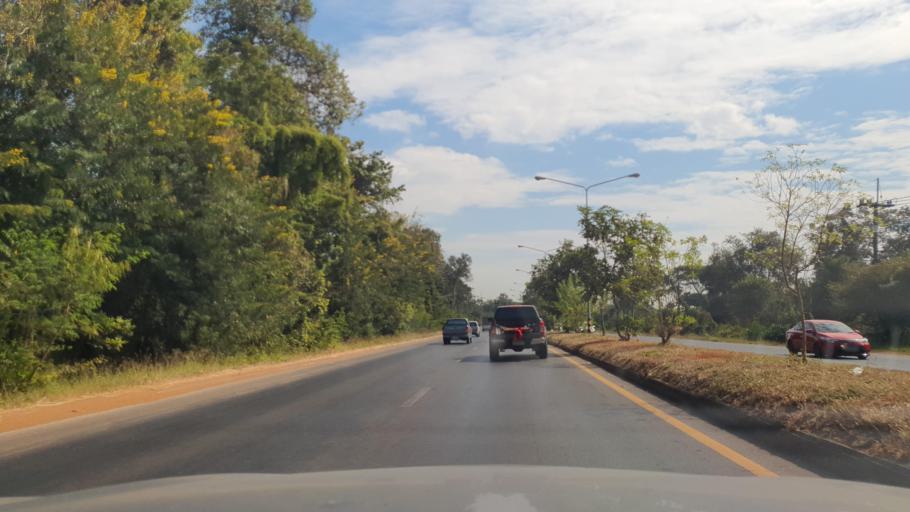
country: TH
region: Kalasin
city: Yang Talat
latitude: 16.4057
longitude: 103.4236
